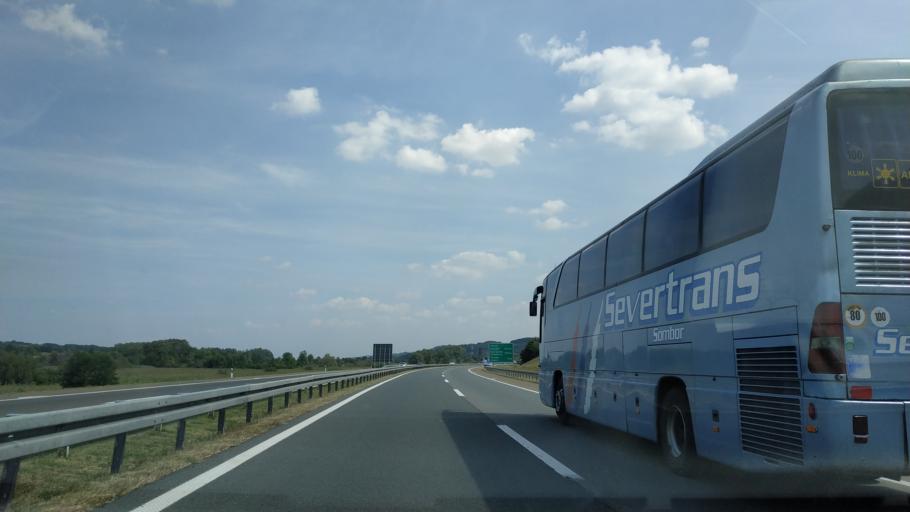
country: RS
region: Central Serbia
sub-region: Belgrade
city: Grocka
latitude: 44.5670
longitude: 20.6789
